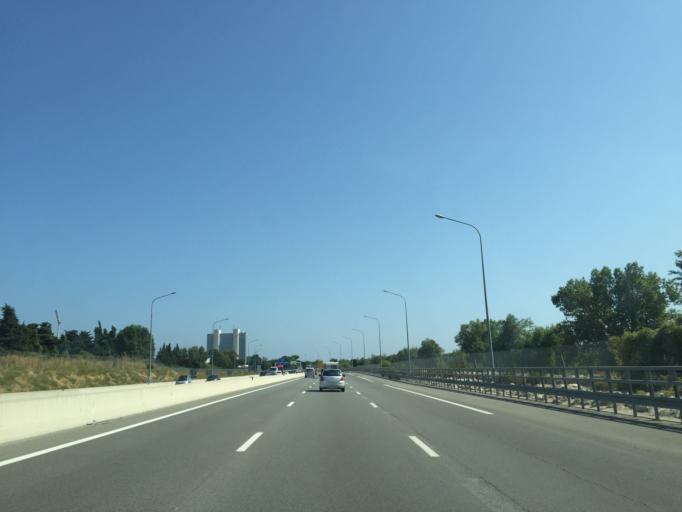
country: FR
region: Provence-Alpes-Cote d'Azur
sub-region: Departement des Alpes-Maritimes
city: Saint-Laurent-du-Var
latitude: 43.6808
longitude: 7.1931
